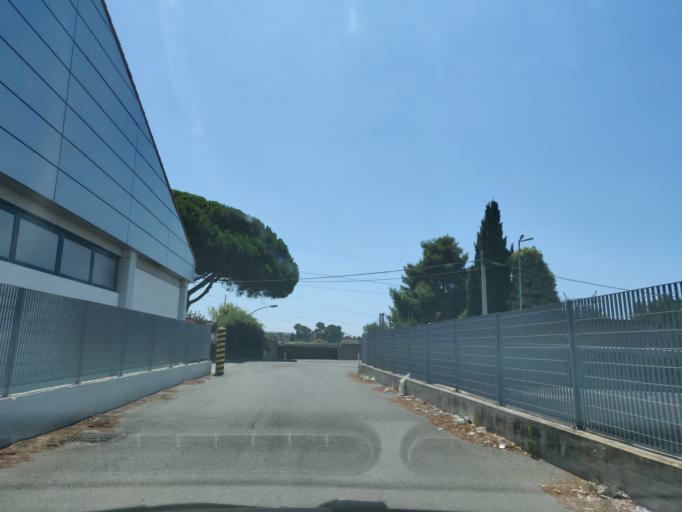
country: IT
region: Latium
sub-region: Citta metropolitana di Roma Capitale
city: Civitavecchia
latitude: 42.1065
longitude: 11.7870
